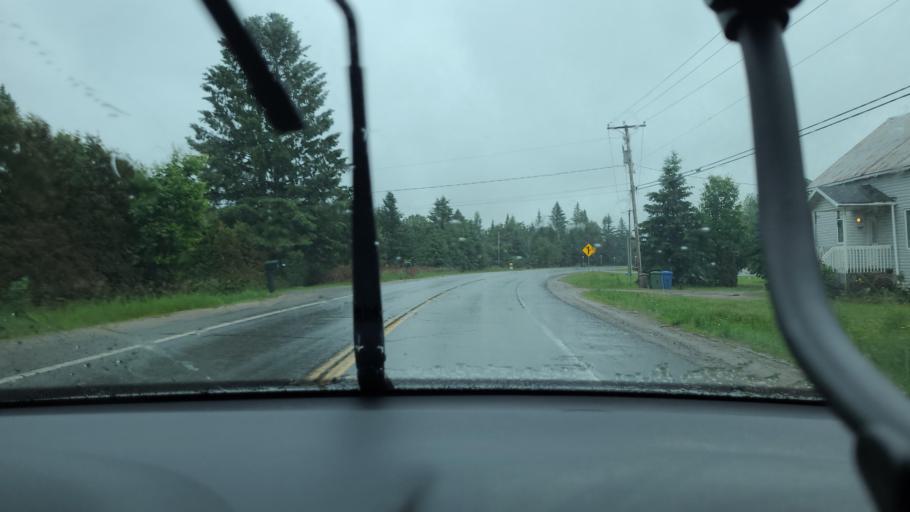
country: CA
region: Quebec
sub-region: Outaouais
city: Saint-Andre-Avellin
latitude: 45.8015
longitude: -75.0641
